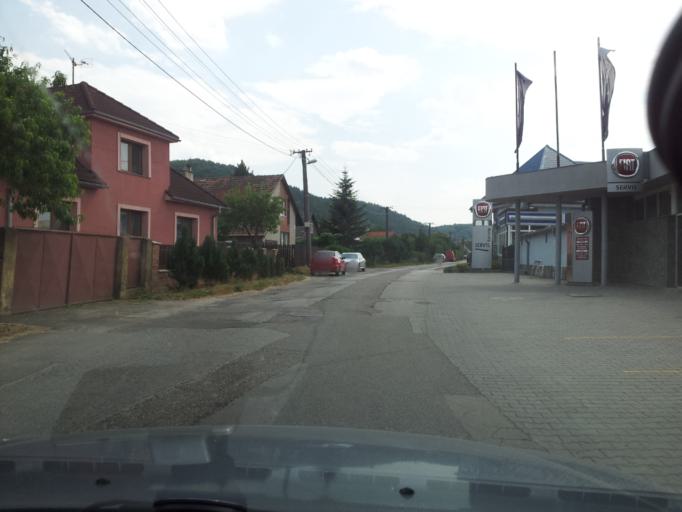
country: SK
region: Trenciansky
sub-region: Okres Trencin
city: Trencin
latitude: 48.8981
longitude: 18.0843
